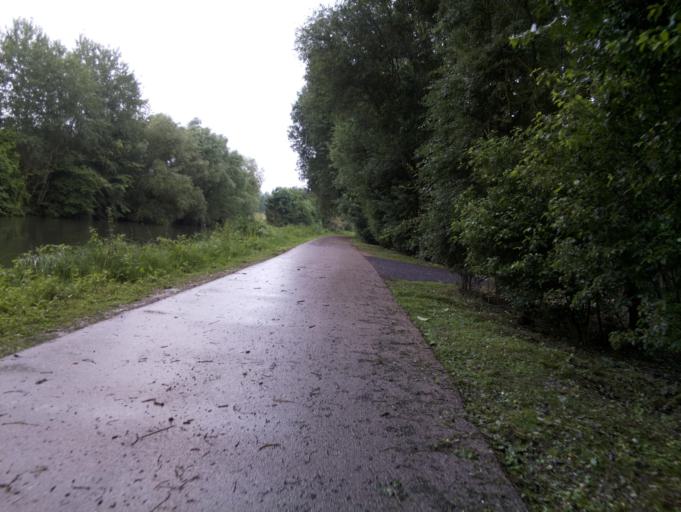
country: FR
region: Picardie
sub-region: Departement de la Somme
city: Ailly-sur-Somme
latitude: 49.9415
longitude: 2.1772
